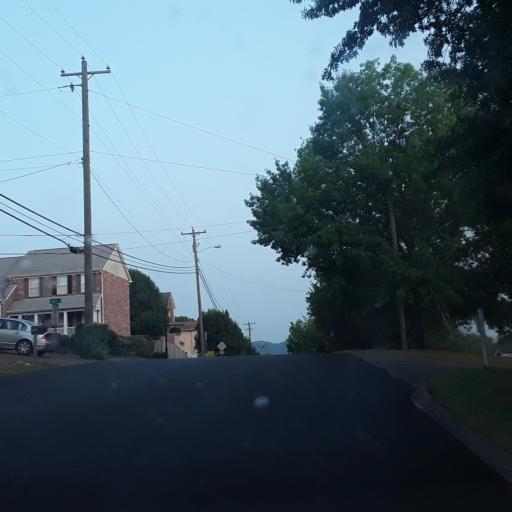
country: US
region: Tennessee
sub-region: Williamson County
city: Brentwood Estates
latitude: 36.0450
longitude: -86.7284
